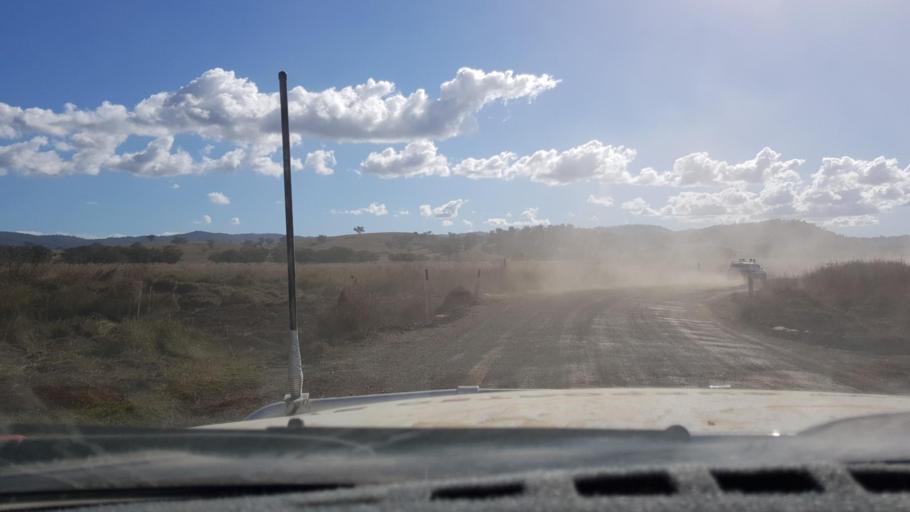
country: AU
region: New South Wales
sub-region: Narrabri
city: Blair Athol
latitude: -30.6743
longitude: 150.4486
